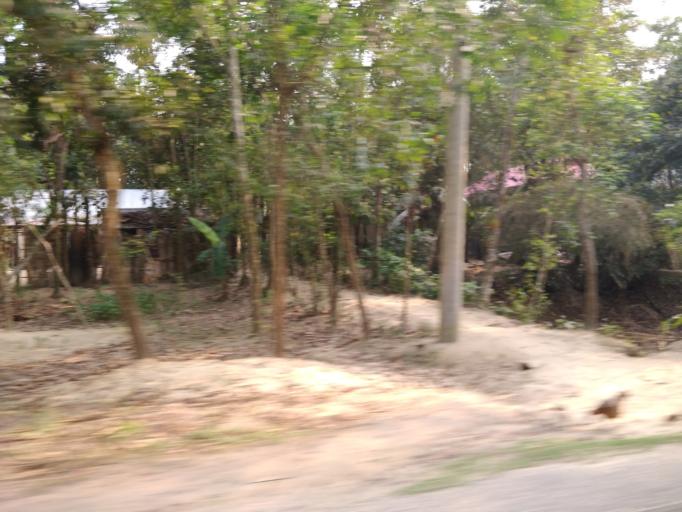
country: IN
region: Tripura
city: Khowai
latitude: 24.1296
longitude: 91.3768
